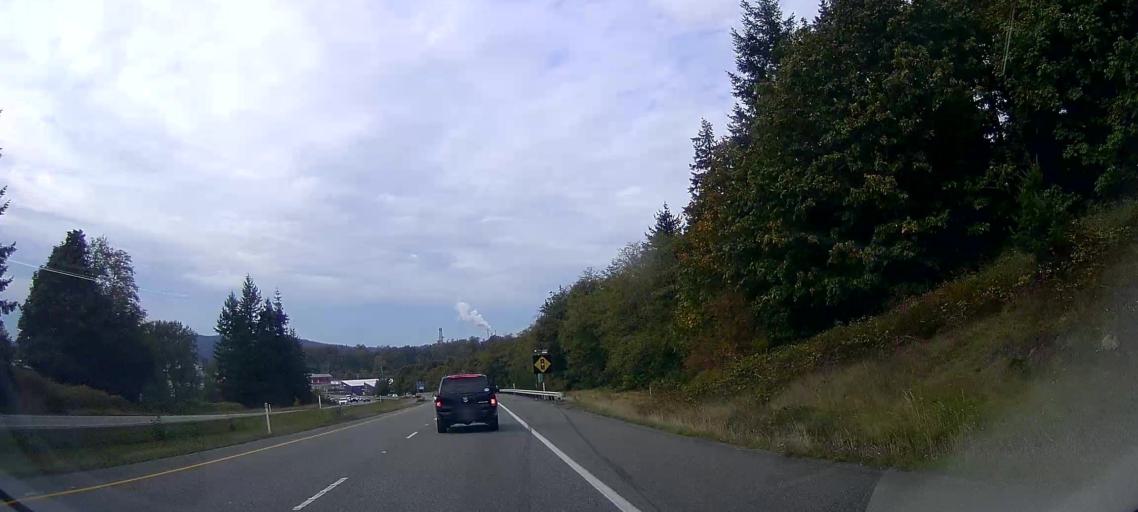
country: US
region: Washington
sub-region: Skagit County
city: Anacortes
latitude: 48.4624
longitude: -122.5372
